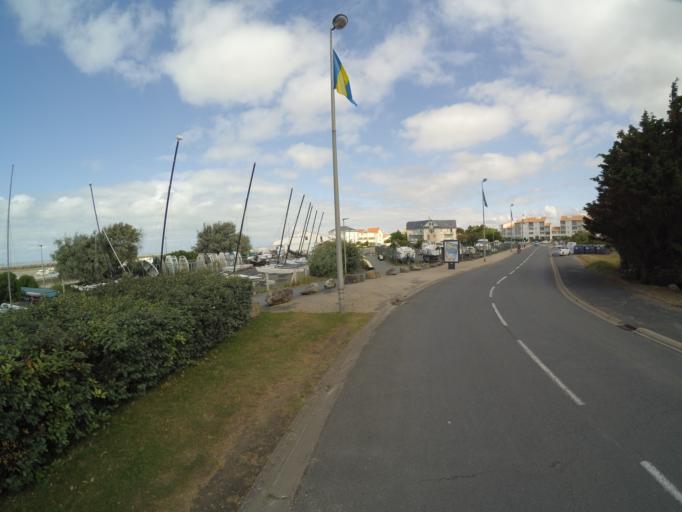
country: FR
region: Poitou-Charentes
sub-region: Departement de la Charente-Maritime
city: Chatelaillon-Plage
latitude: 46.0614
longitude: -1.0912
